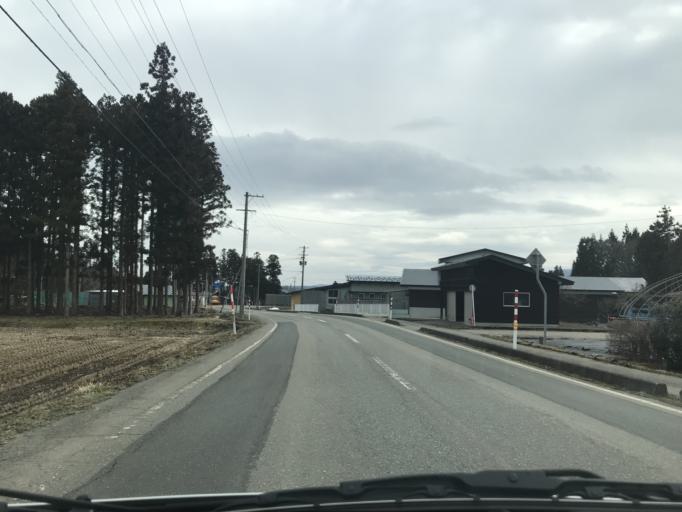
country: JP
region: Iwate
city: Kitakami
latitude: 39.3302
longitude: 140.9762
